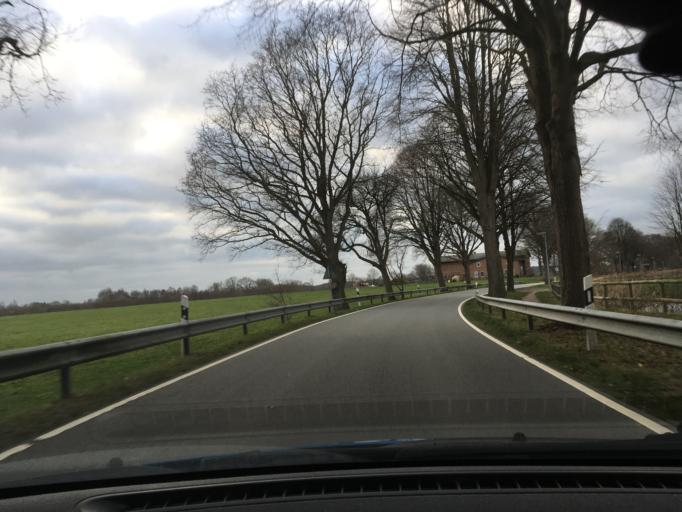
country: DE
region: Schleswig-Holstein
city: Hadenfeld
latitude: 54.0466
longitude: 9.4657
